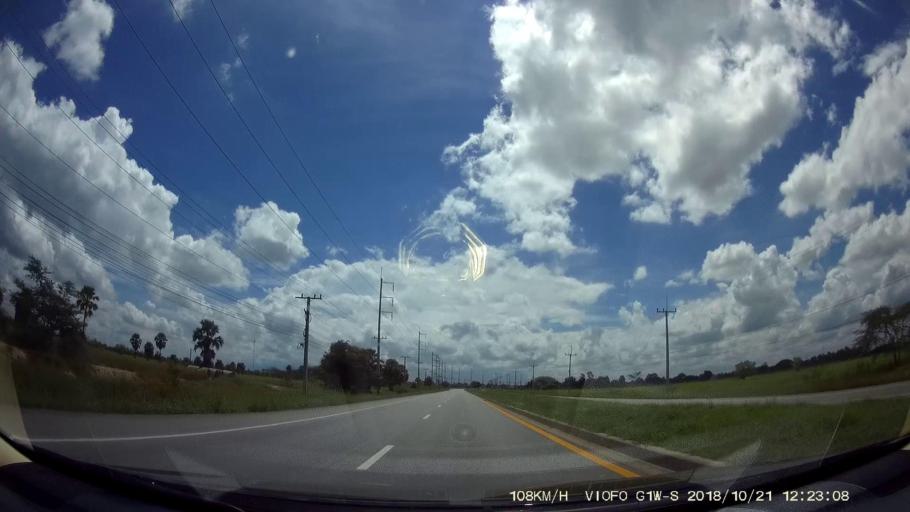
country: TH
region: Nakhon Ratchasima
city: Dan Khun Thot
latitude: 15.2500
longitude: 101.7888
